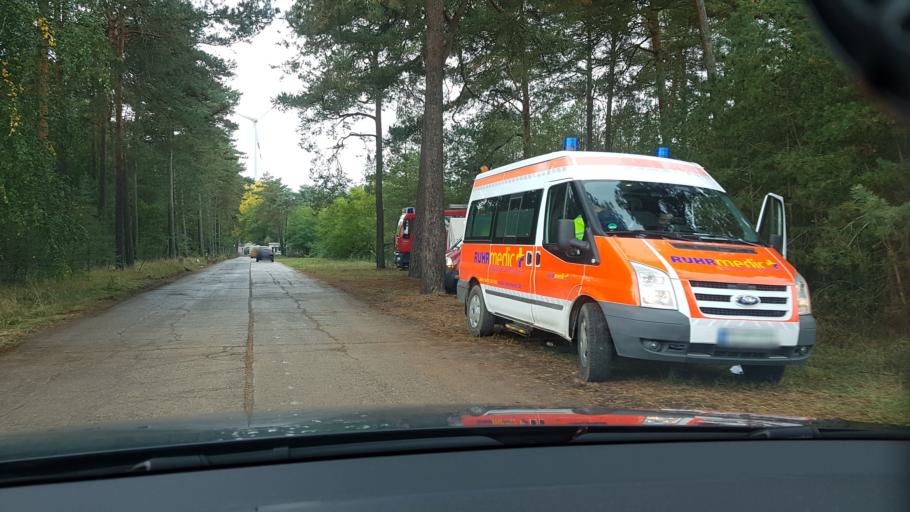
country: DE
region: Saxony-Anhalt
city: Tangerhutte
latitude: 52.3773
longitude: 11.8300
